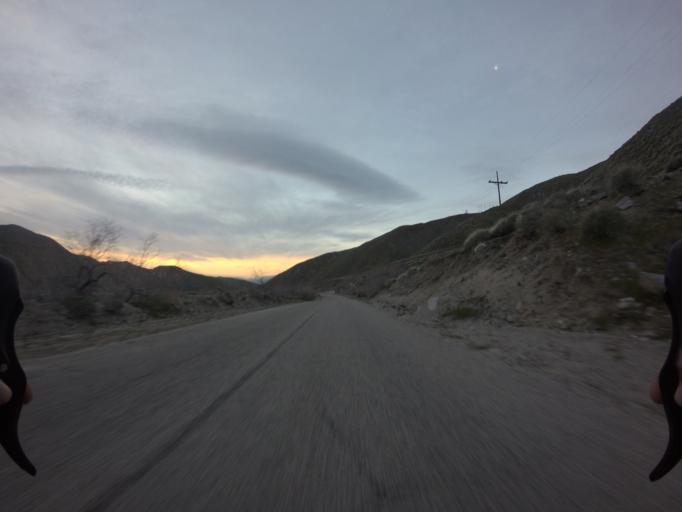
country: US
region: California
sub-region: San Bernardino County
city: Morongo Valley
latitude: 33.9662
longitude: -116.6518
